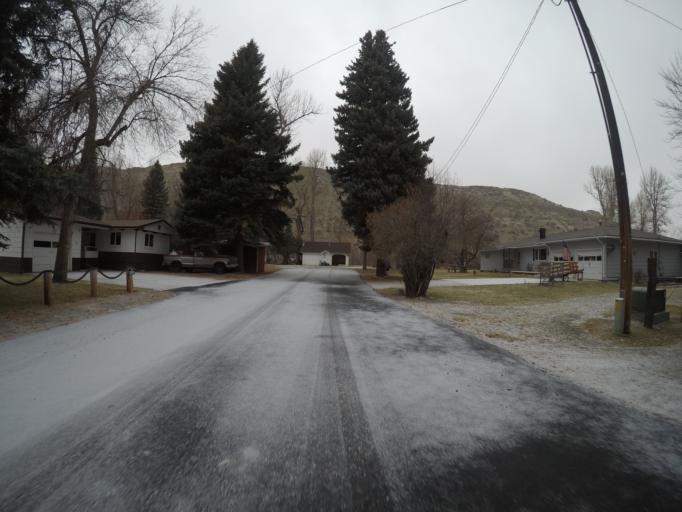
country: US
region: Montana
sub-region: Stillwater County
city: Absarokee
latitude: 45.5188
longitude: -109.4486
